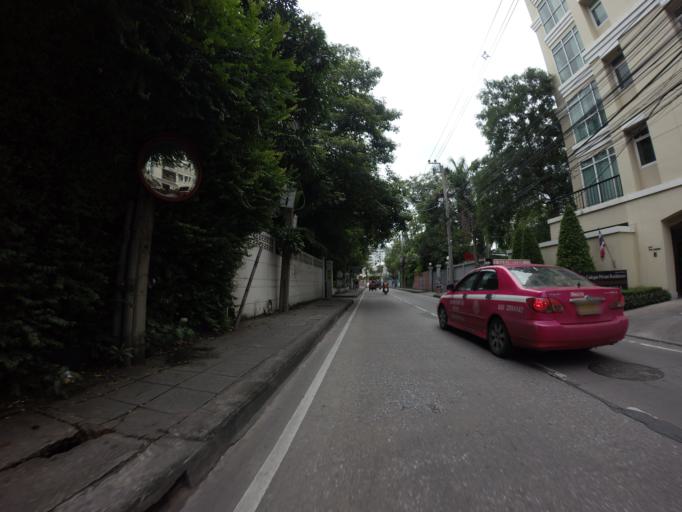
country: TH
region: Bangkok
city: Watthana
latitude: 13.7408
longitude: 100.5727
